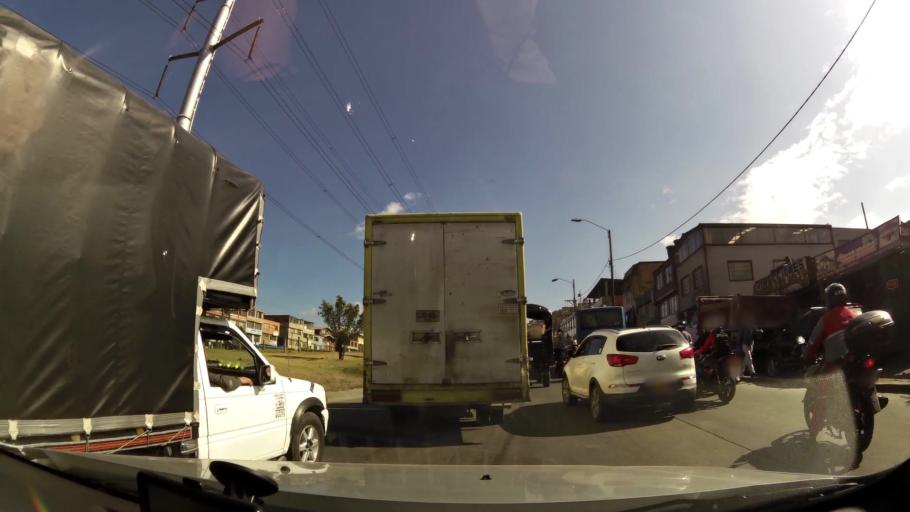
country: CO
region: Bogota D.C.
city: Bogota
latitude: 4.5627
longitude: -74.1390
